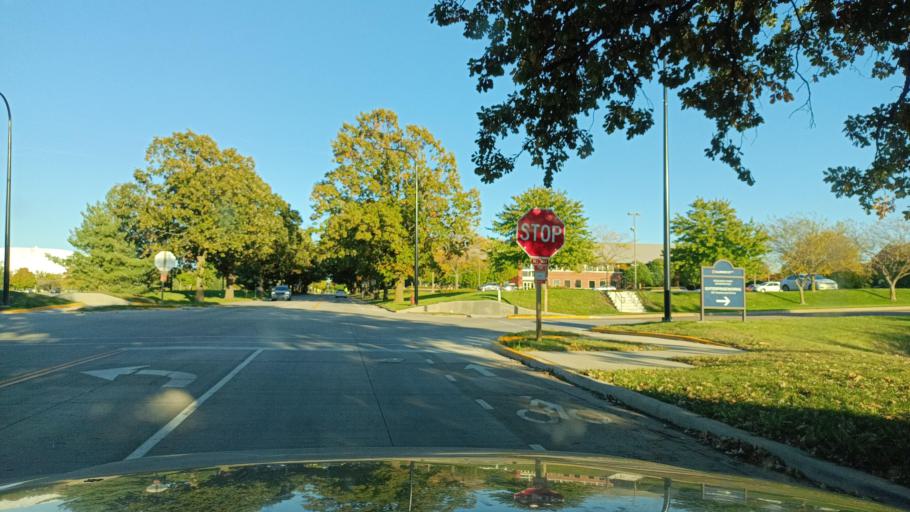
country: US
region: Illinois
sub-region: Champaign County
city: Champaign
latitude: 40.0945
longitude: -88.2419
